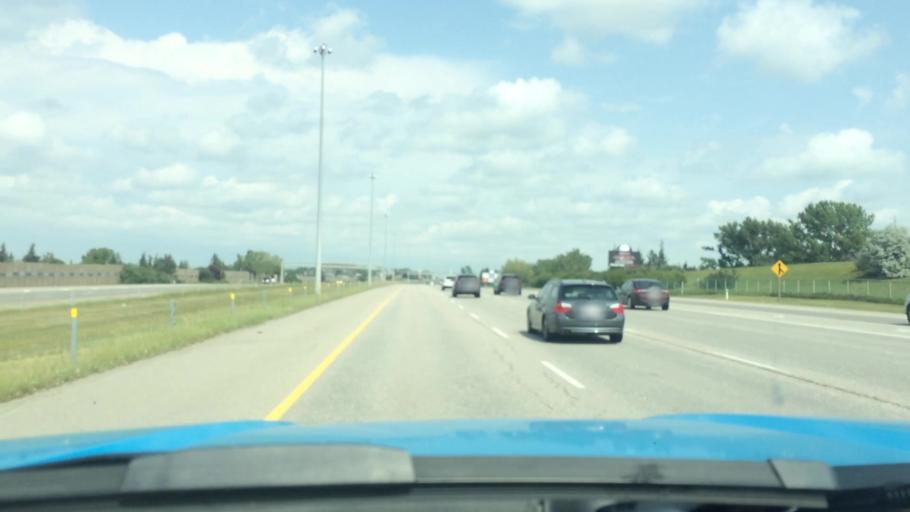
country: CA
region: Alberta
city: Airdrie
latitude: 51.2739
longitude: -114.0014
